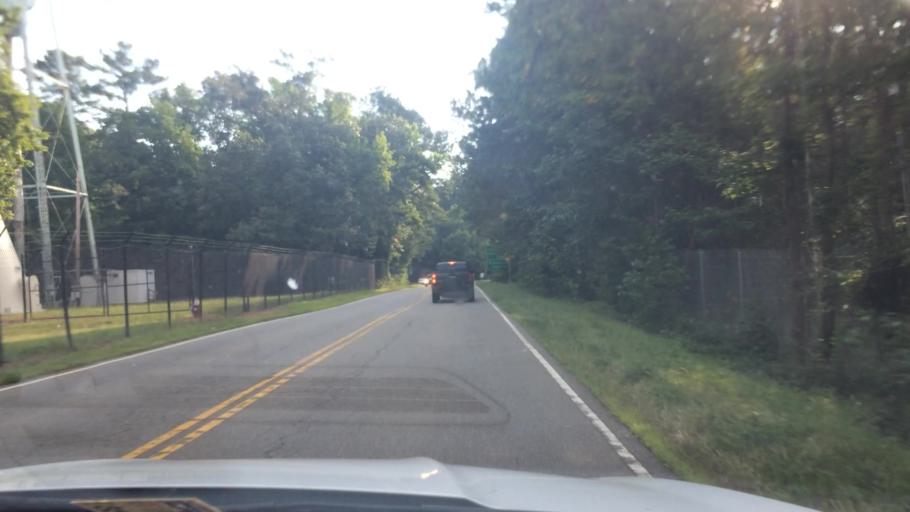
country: US
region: Virginia
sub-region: City of Williamsburg
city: Williamsburg
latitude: 37.2798
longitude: -76.6296
